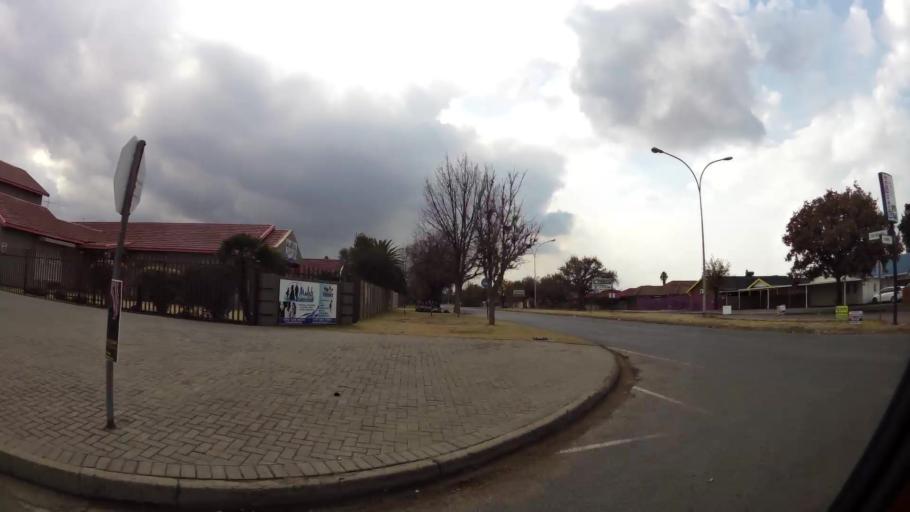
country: ZA
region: Gauteng
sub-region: Sedibeng District Municipality
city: Vanderbijlpark
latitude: -26.7246
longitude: 27.8527
